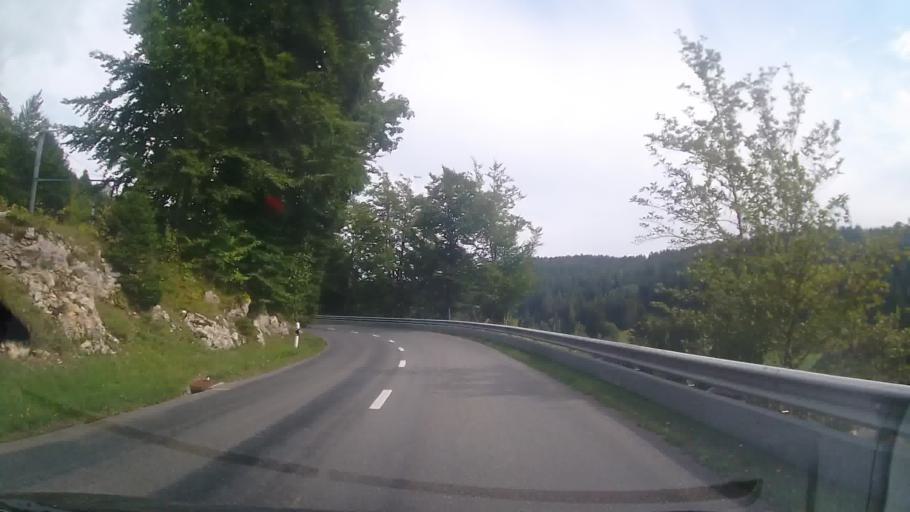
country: CH
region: Vaud
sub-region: Nyon District
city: Saint-Cergue
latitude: 46.4487
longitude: 6.1351
